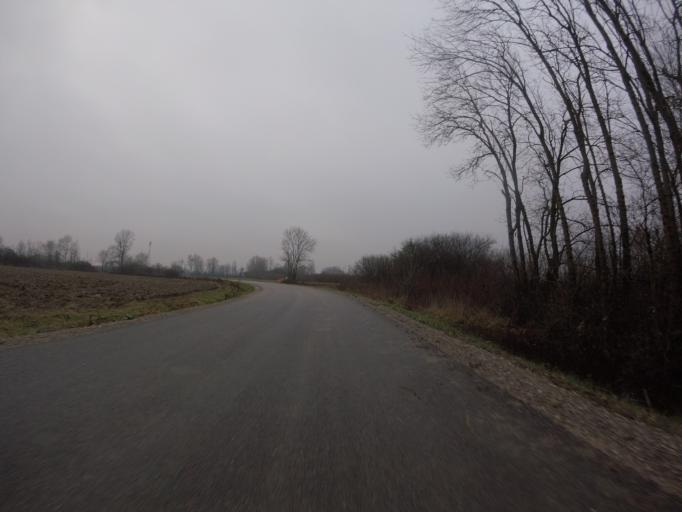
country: HR
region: Sisacko-Moslavacka
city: Lekenik
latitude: 45.6468
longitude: 16.2778
